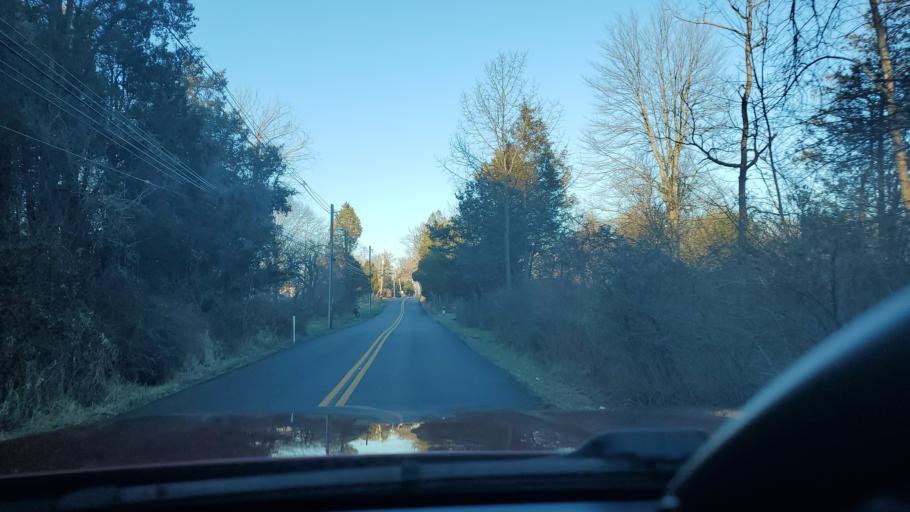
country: US
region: Pennsylvania
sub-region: Montgomery County
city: Woxall
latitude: 40.3117
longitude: -75.4976
